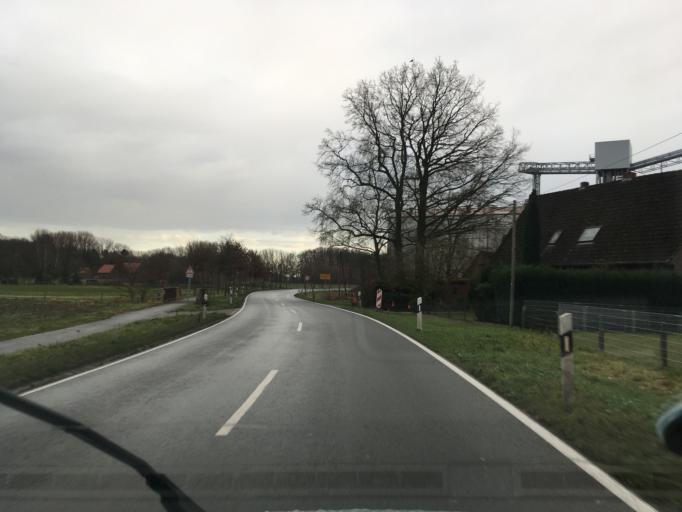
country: DE
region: North Rhine-Westphalia
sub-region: Regierungsbezirk Munster
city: Schoppingen
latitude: 52.0889
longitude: 7.2131
